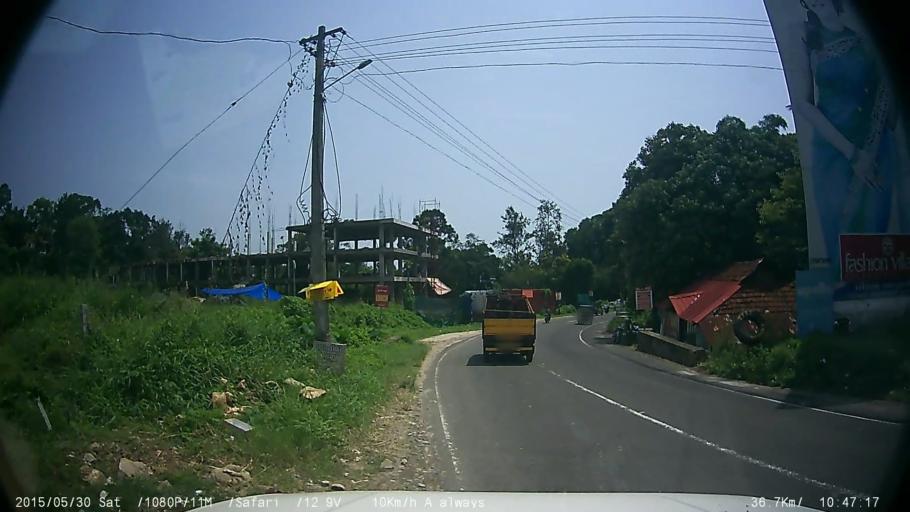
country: IN
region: Kerala
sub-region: Wayanad
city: Kalpetta
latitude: 11.6298
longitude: 76.0890
